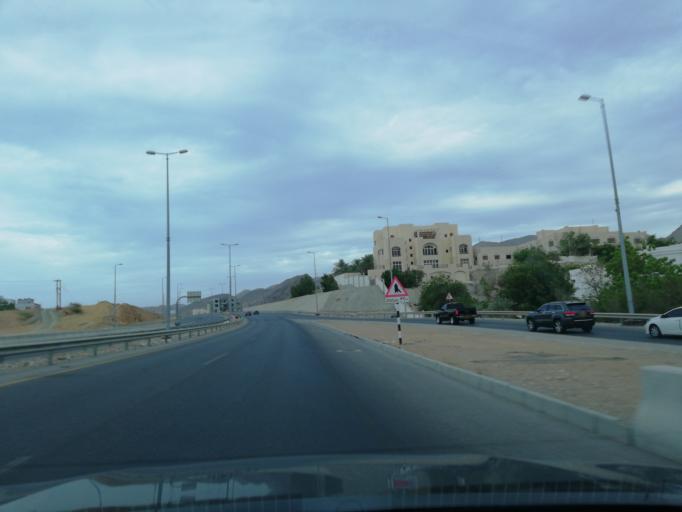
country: OM
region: Muhafazat Masqat
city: Bawshar
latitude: 23.5906
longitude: 58.4498
